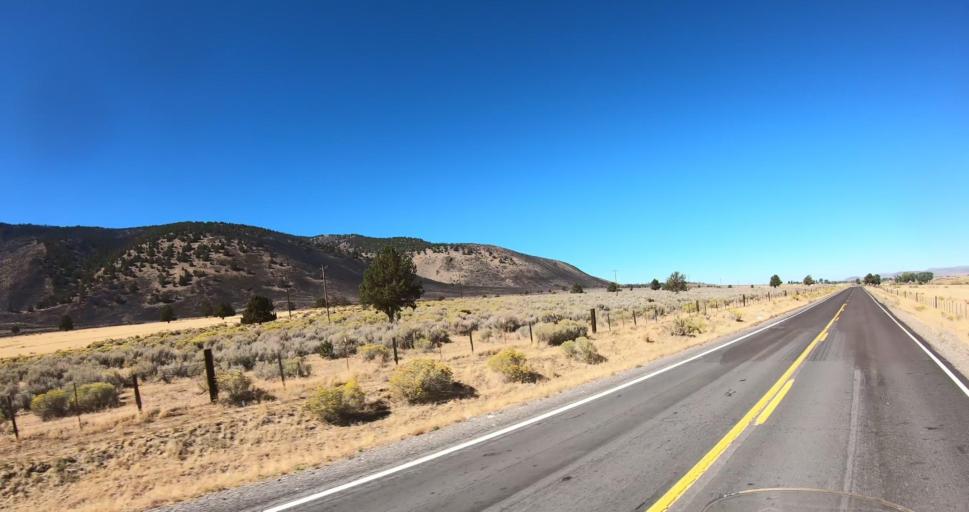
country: US
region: Oregon
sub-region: Lake County
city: Lakeview
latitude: 42.6481
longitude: -120.5214
